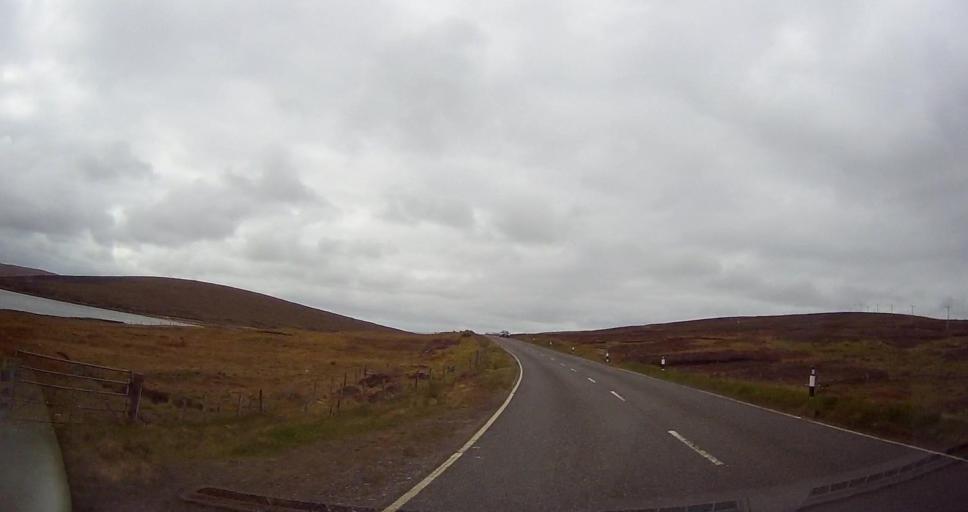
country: GB
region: Scotland
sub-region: Shetland Islands
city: Lerwick
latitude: 60.2494
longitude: -1.3728
